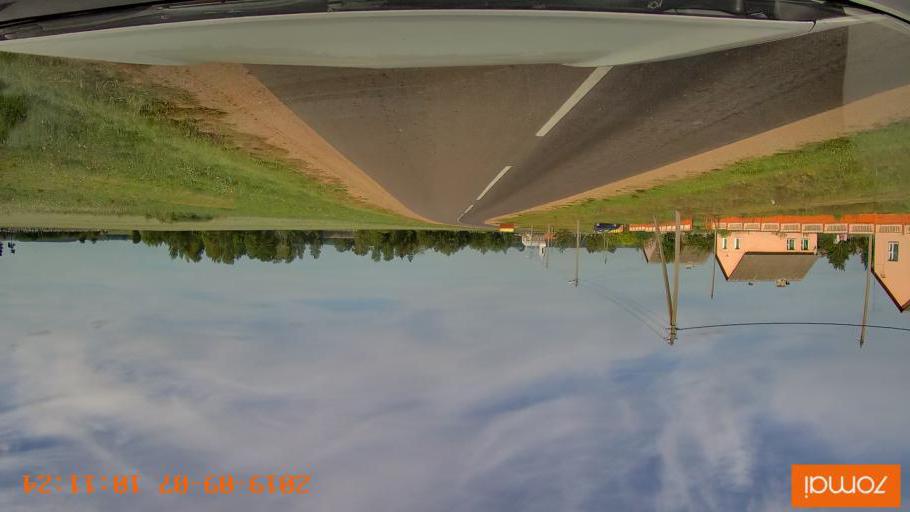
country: BY
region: Grodnenskaya
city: Voranava
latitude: 54.1227
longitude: 25.3663
